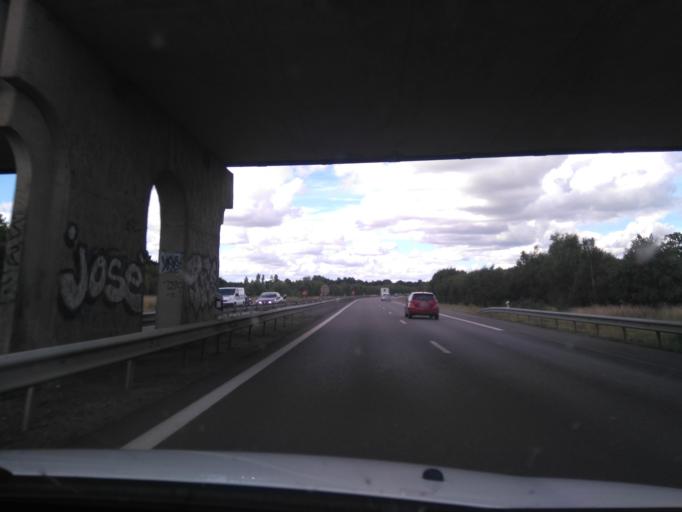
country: FR
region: Brittany
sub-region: Departement d'Ille-et-Vilaine
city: Laille
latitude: 47.9907
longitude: -1.6955
